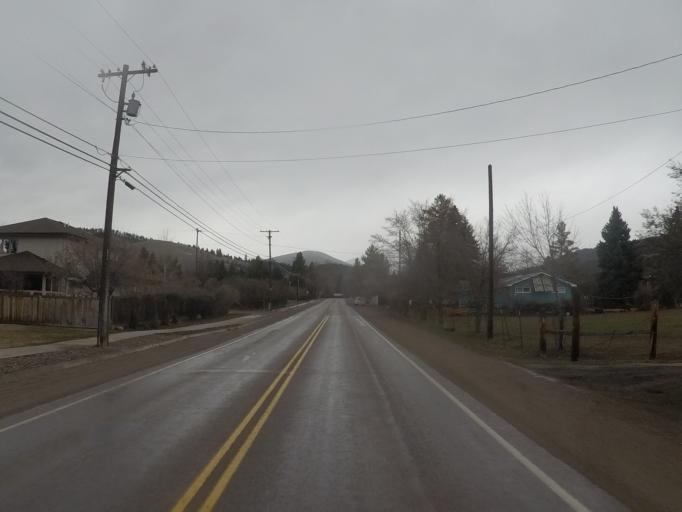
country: US
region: Montana
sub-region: Missoula County
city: East Missoula
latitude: 46.8972
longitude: -113.9656
